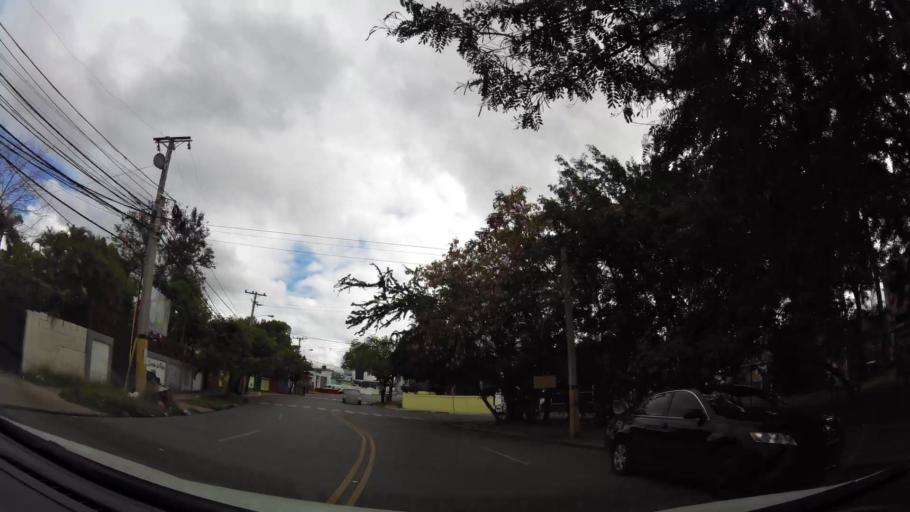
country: DO
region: Nacional
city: Bella Vista
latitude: 18.4760
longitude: -69.9607
